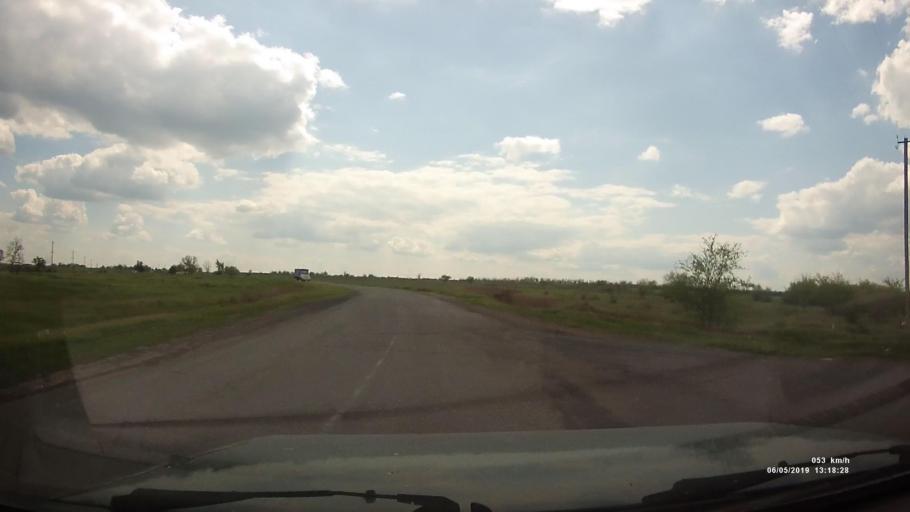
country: RU
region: Rostov
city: Ust'-Donetskiy
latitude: 47.7334
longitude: 40.9147
